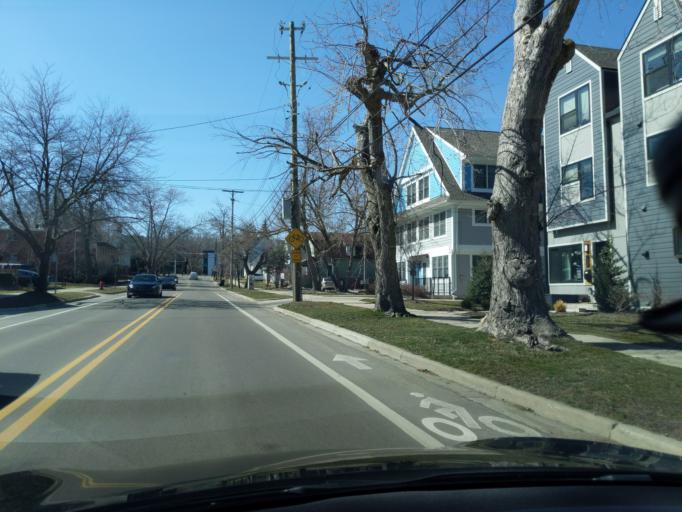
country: US
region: Michigan
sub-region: Washtenaw County
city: Ann Arbor
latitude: 42.2717
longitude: -83.7479
